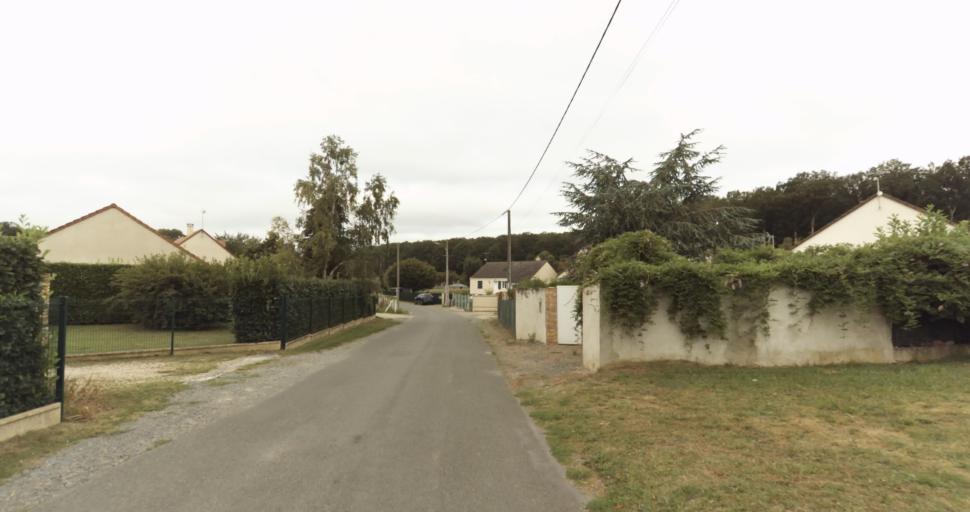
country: FR
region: Haute-Normandie
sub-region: Departement de l'Eure
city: Saint-Germain-sur-Avre
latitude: 48.7797
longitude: 1.2605
